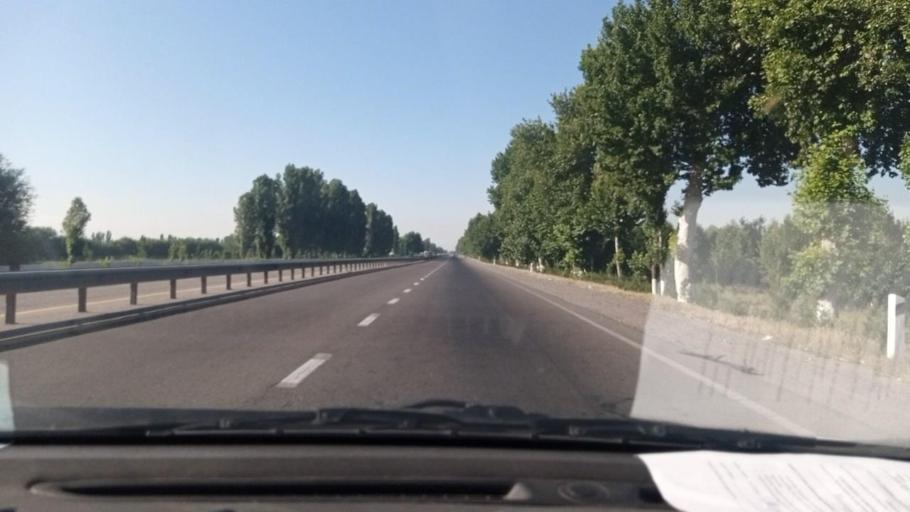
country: UZ
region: Toshkent Shahri
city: Bektemir
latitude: 41.2149
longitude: 69.4026
